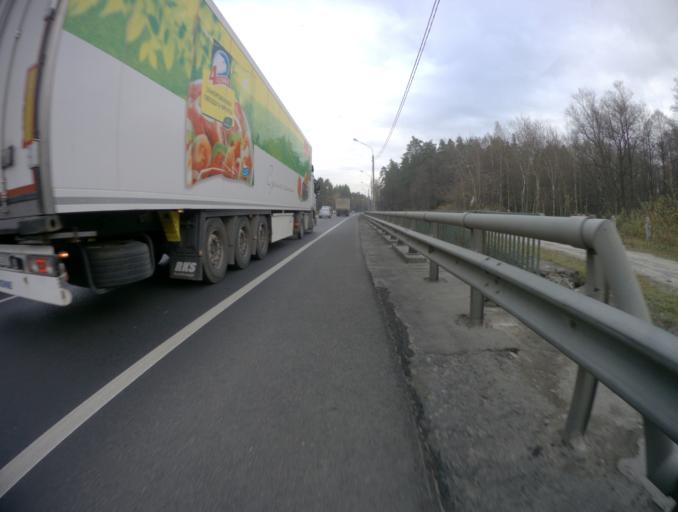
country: RU
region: Moskovskaya
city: Malaya Dubna
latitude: 55.8617
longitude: 38.9626
